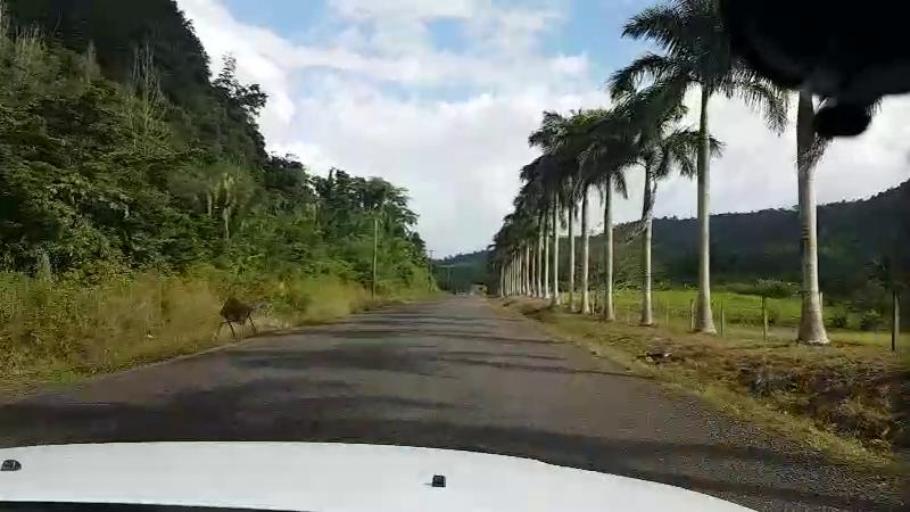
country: BZ
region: Cayo
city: Belmopan
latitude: 17.0907
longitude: -88.6230
